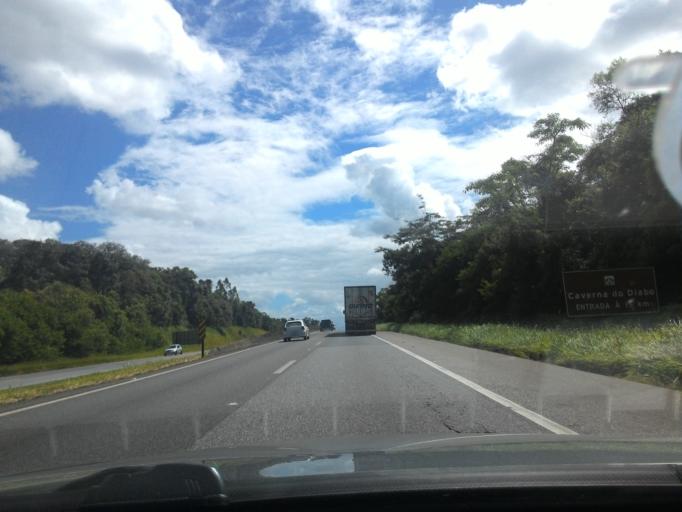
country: BR
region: Sao Paulo
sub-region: Pariquera-Acu
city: Pariquera Acu
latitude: -24.6138
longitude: -47.8866
